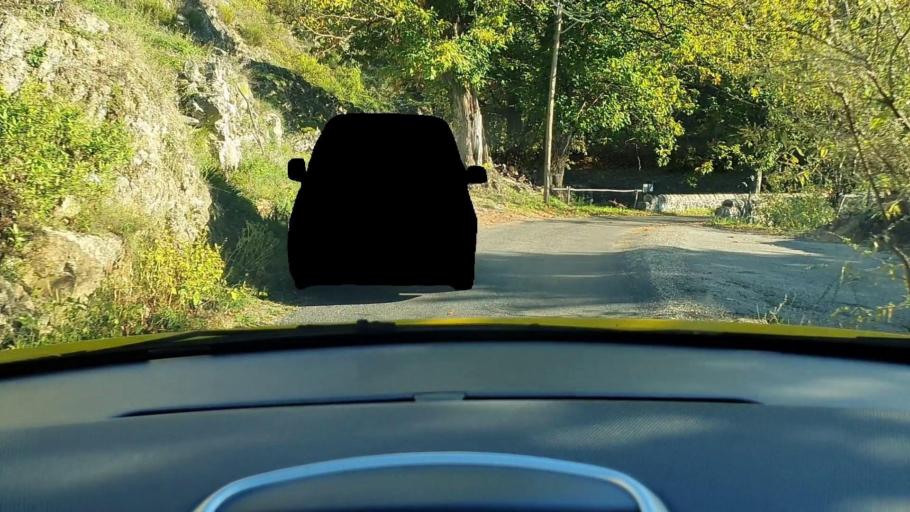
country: FR
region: Languedoc-Roussillon
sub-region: Departement du Gard
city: Sumene
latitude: 44.0182
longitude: 3.7771
